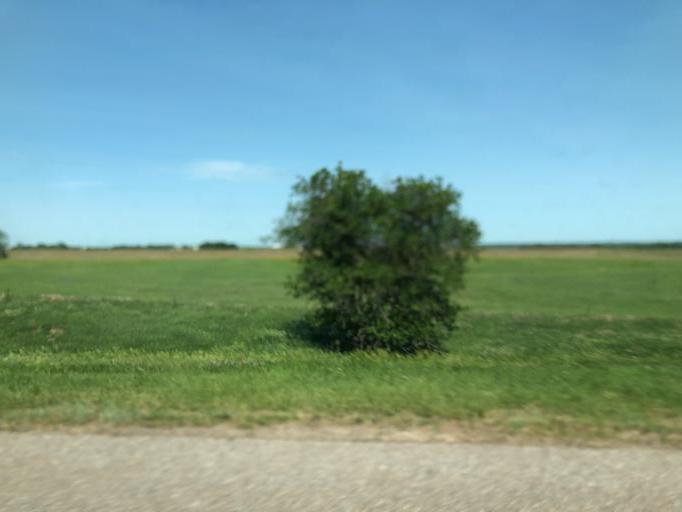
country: US
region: Nebraska
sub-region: York County
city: York
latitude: 40.7655
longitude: -97.5975
